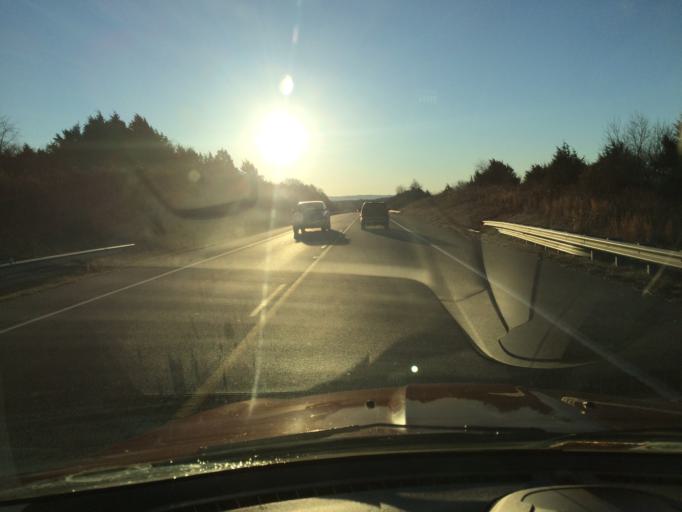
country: US
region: Virginia
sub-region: Augusta County
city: Verona
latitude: 38.1756
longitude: -79.0240
